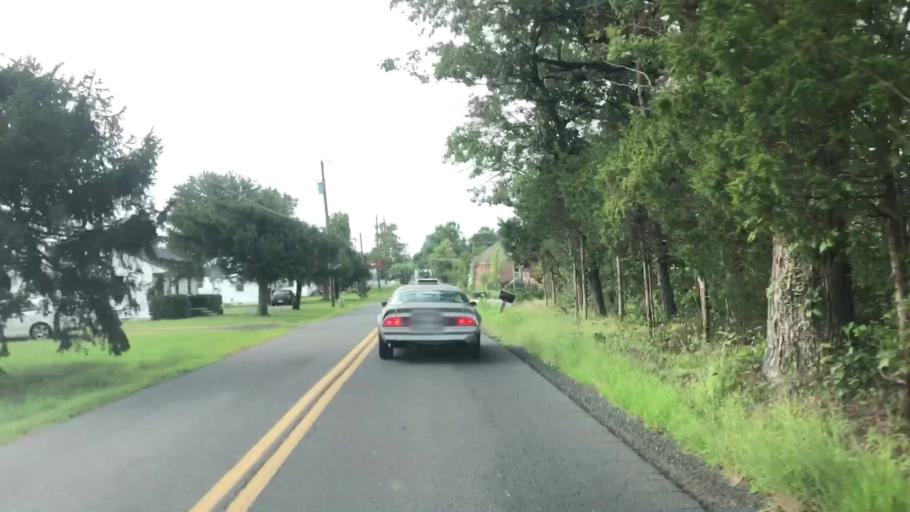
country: US
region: Virginia
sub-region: Prince William County
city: Gainesville
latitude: 38.7474
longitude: -77.6482
